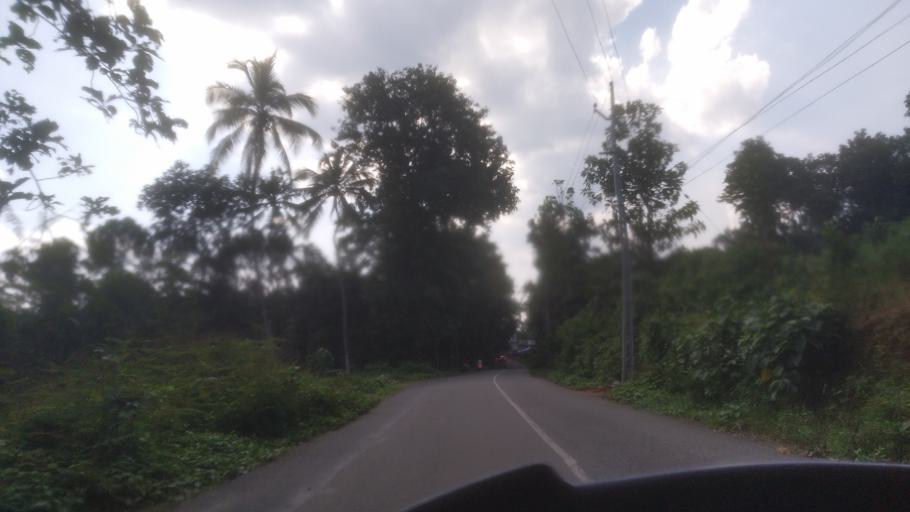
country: IN
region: Kerala
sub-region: Ernakulam
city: Kotamangalam
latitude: 10.0051
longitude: 76.6698
